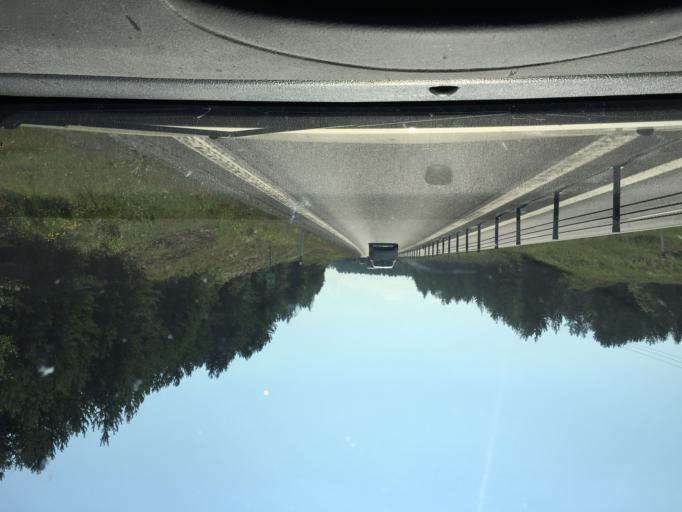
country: SE
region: Norrbotten
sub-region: Lulea Kommun
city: Gammelstad
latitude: 65.6023
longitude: 22.0499
